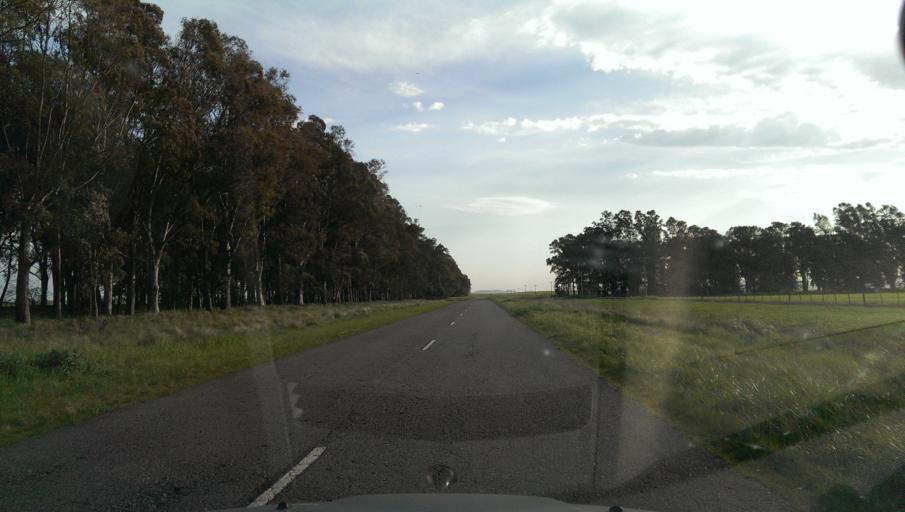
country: AR
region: Buenos Aires
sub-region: Partido de Coronel Suarez
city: Coronel Suarez
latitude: -37.8261
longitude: -61.8159
